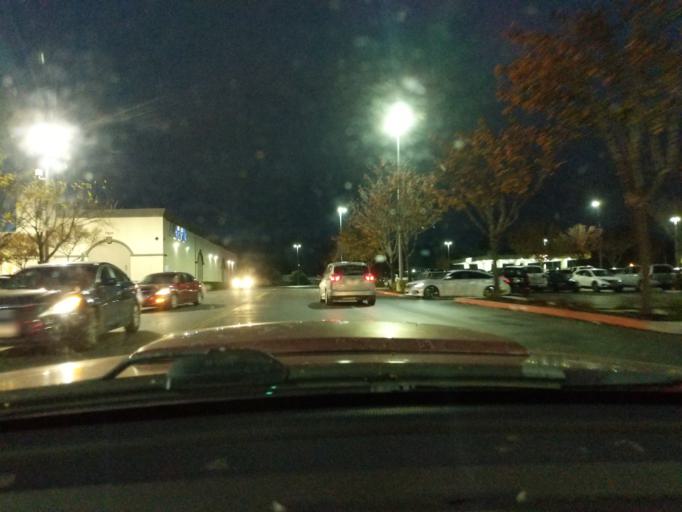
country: US
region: California
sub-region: Santa Clara County
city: Gilroy
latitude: 37.0075
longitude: -121.5547
